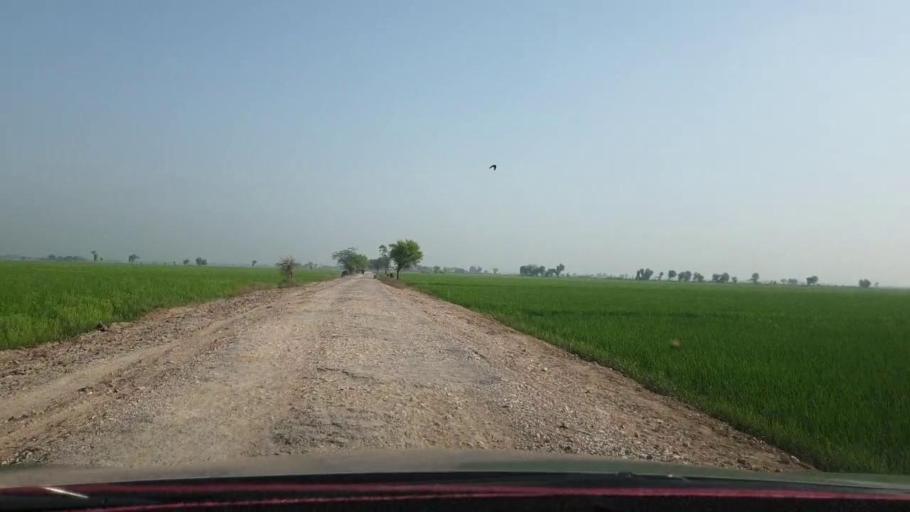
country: PK
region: Sindh
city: Nasirabad
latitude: 27.4672
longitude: 67.9213
